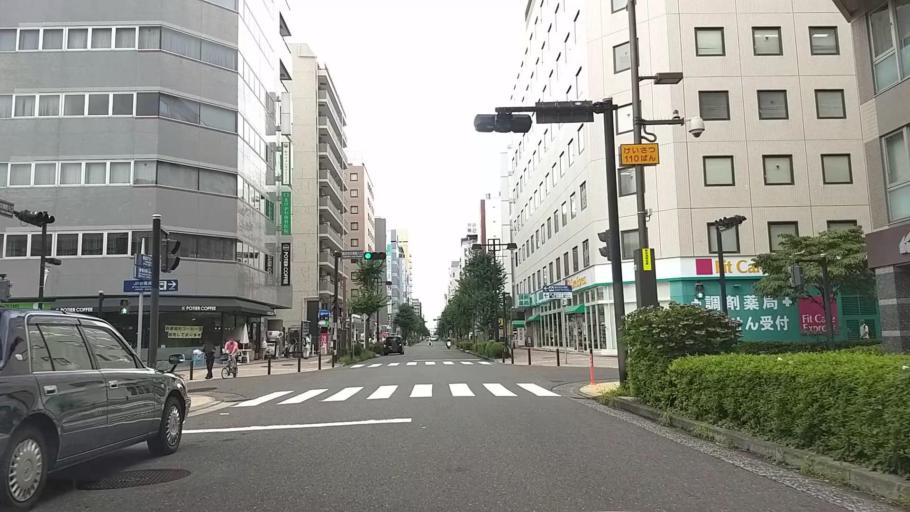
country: JP
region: Kanagawa
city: Yokohama
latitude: 35.5079
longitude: 139.6129
